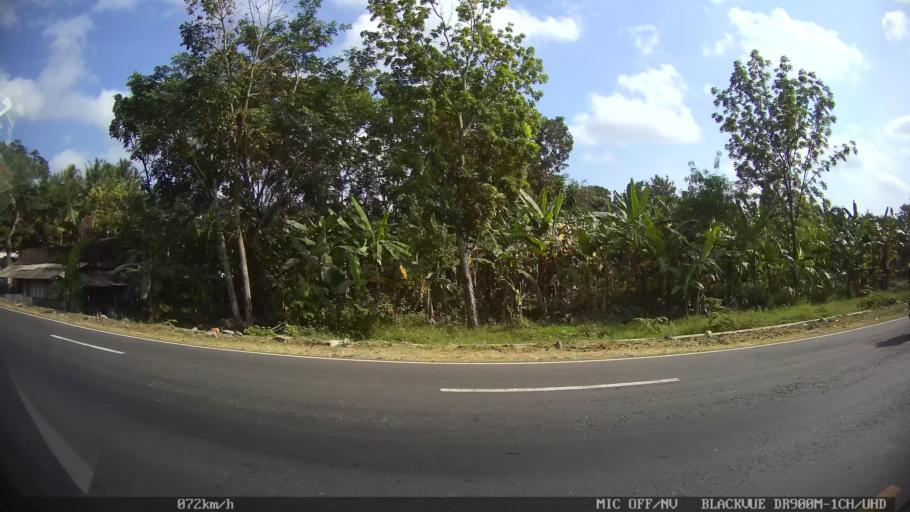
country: ID
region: Daerah Istimewa Yogyakarta
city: Godean
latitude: -7.8165
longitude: 110.2492
